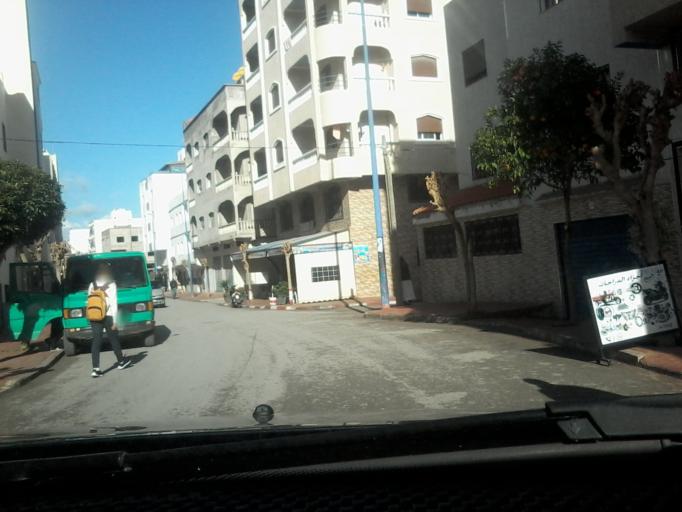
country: MA
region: Tanger-Tetouan
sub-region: Tetouan
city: Martil
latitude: 35.6844
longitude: -5.3266
